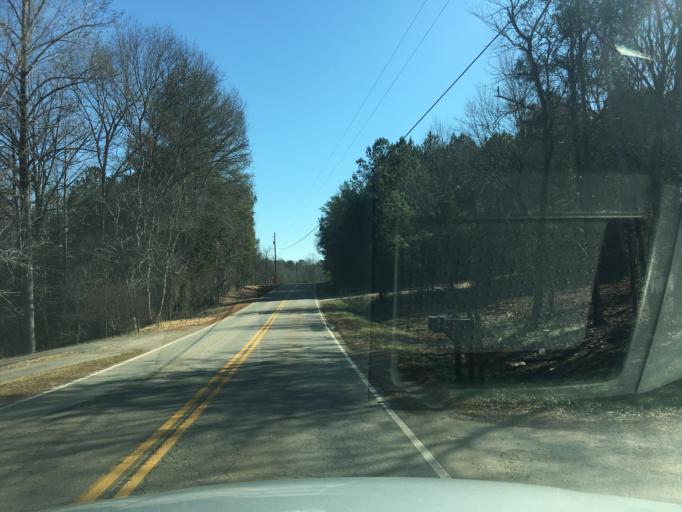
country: US
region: South Carolina
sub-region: Pickens County
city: Liberty
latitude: 34.7965
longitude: -82.7349
